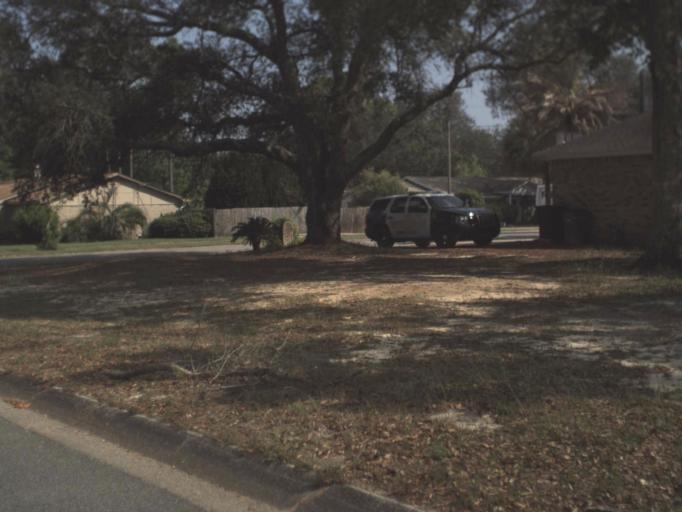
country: US
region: Florida
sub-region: Escambia County
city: Ferry Pass
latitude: 30.4921
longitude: -87.1595
